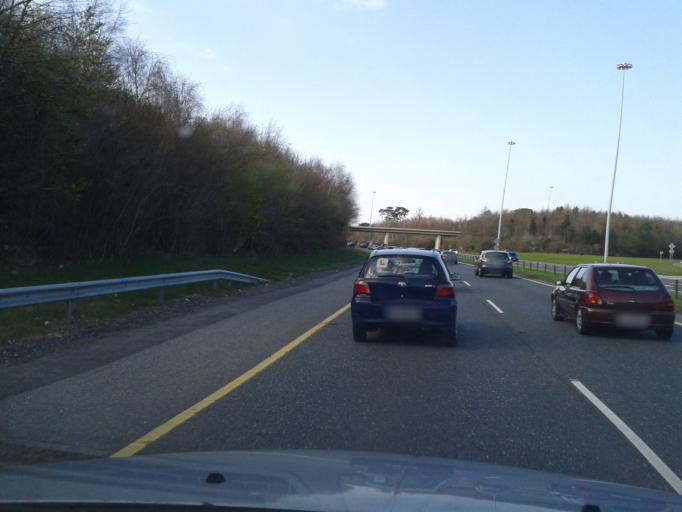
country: IE
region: Leinster
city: Little Bray
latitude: 53.2108
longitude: -6.1246
